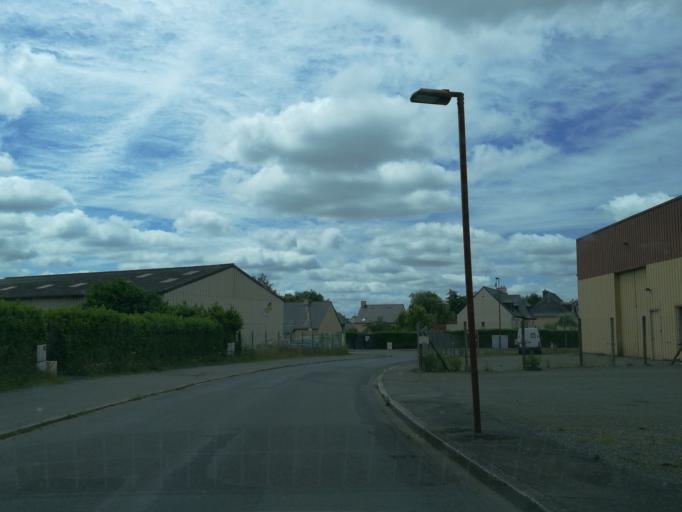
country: FR
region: Brittany
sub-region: Departement d'Ille-et-Vilaine
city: Bedee
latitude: 48.1798
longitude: -1.9334
